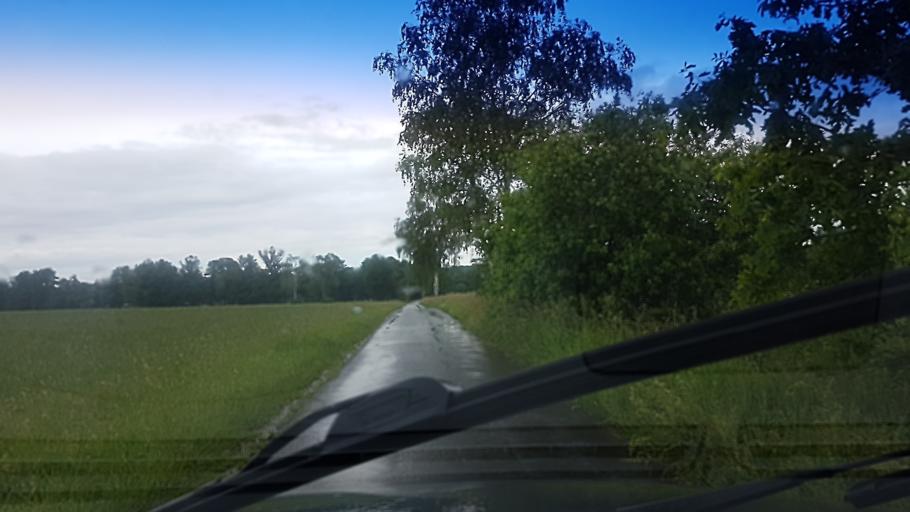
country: DE
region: Bavaria
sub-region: Upper Franconia
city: Gesees
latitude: 50.0302
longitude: 11.6423
